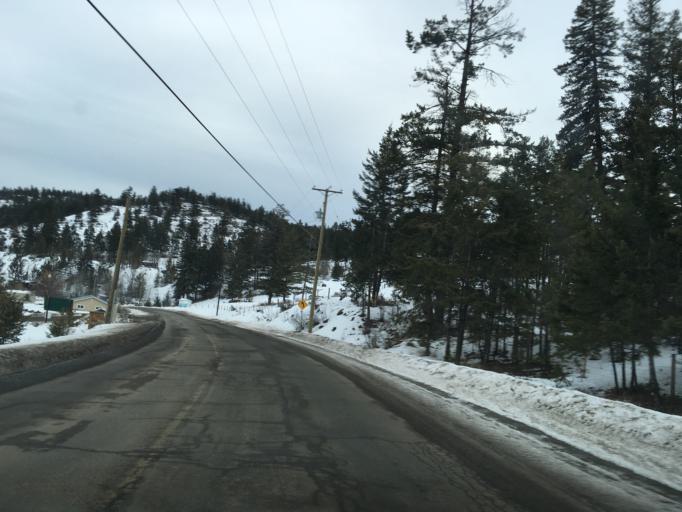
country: CA
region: British Columbia
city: Kamloops
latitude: 50.6553
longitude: -120.4418
